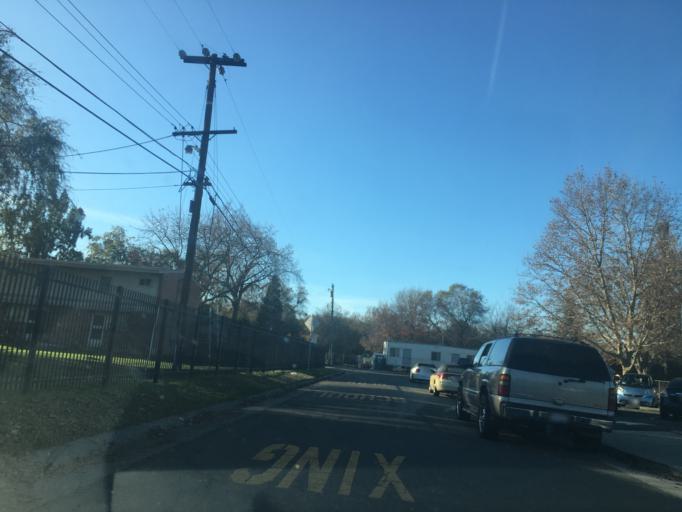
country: US
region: California
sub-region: Yolo County
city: West Sacramento
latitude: 38.5615
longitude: -121.5126
